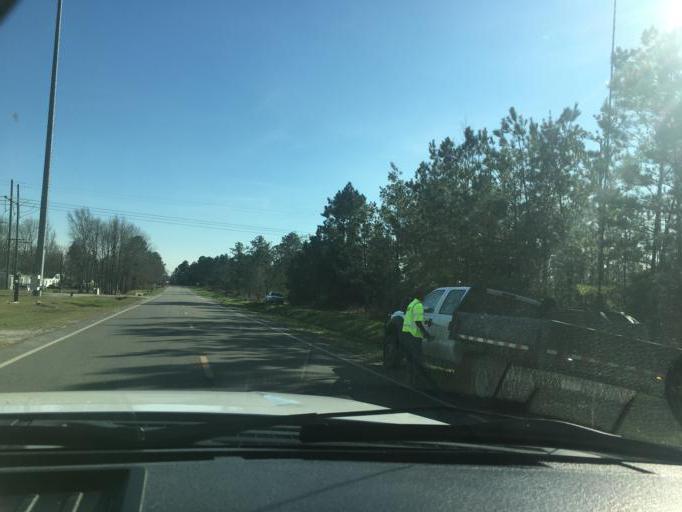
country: US
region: Alabama
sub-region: Lee County
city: Opelika
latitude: 32.4731
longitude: -85.3670
